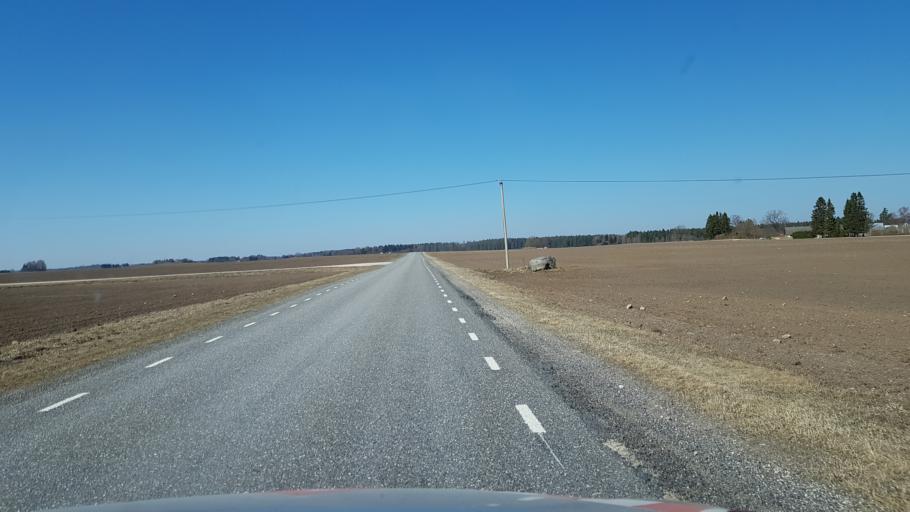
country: EE
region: Laeaene-Virumaa
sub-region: Rakke vald
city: Rakke
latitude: 59.0039
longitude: 26.1879
